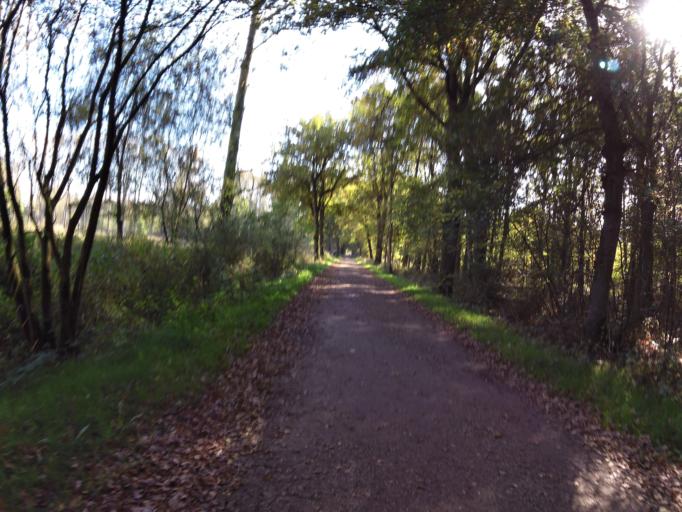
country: NL
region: Limburg
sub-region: Gemeente Weert
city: Weert
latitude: 51.3076
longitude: 5.6705
